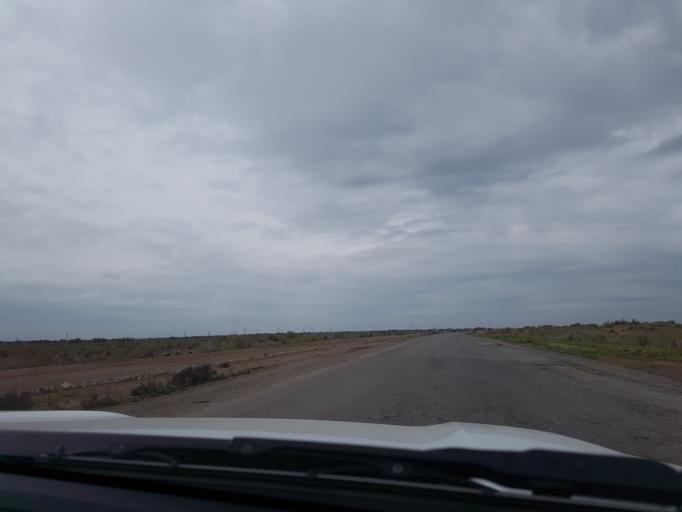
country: TM
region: Mary
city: Bayramaly
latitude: 37.8016
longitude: 62.5599
